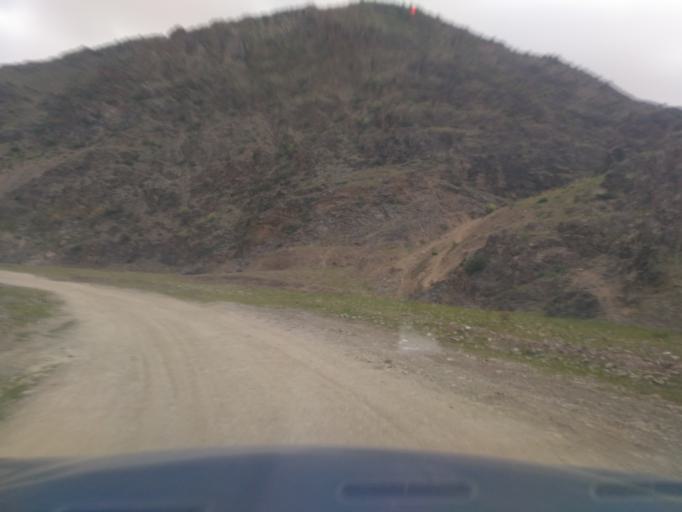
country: UZ
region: Jizzax
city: Zomin
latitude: 39.8516
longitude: 68.3958
